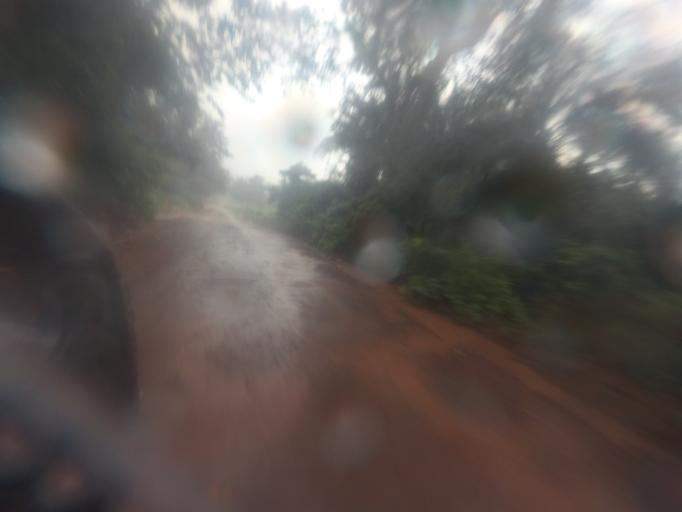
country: SL
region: Northern Province
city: Kambia
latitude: 9.2308
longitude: -12.8088
